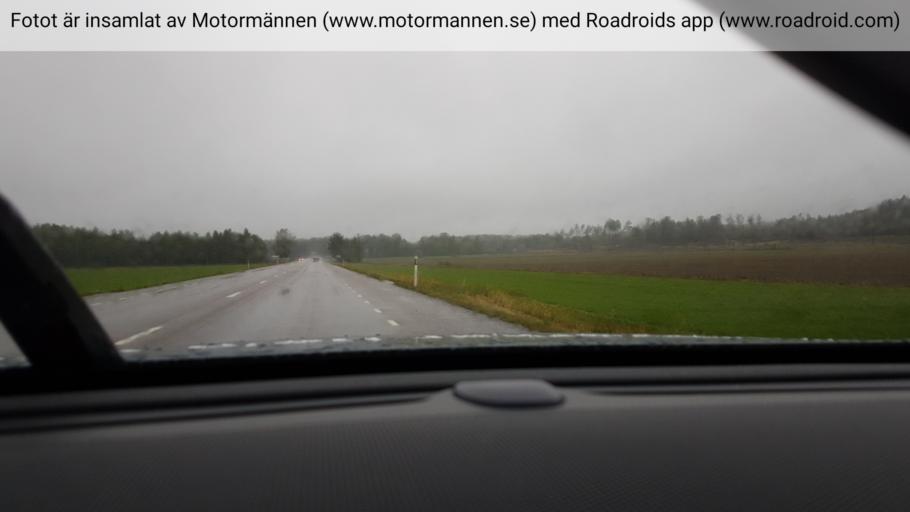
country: SE
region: Vaestra Goetaland
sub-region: Amals Kommun
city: Amal
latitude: 59.0047
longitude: 12.6857
